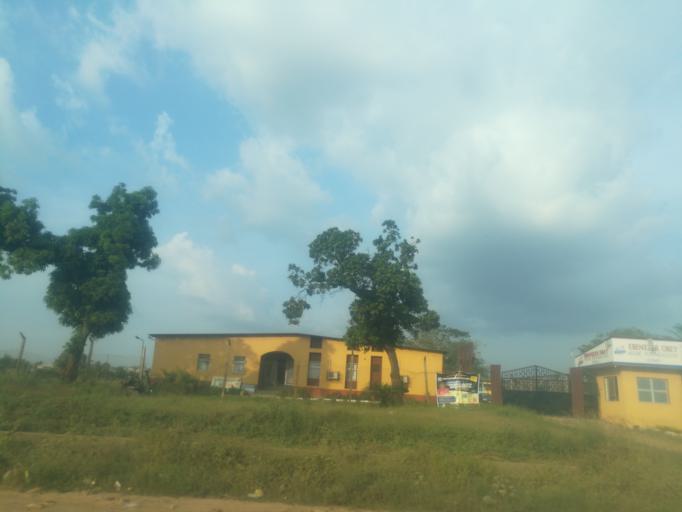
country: NG
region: Ogun
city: Abeokuta
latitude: 7.1694
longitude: 3.2958
